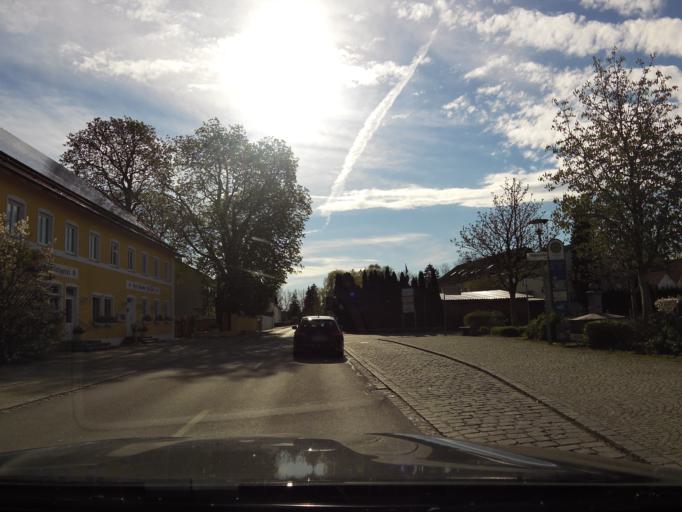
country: DE
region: Bavaria
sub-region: Upper Bavaria
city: Oberding
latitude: 48.3400
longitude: 11.8366
